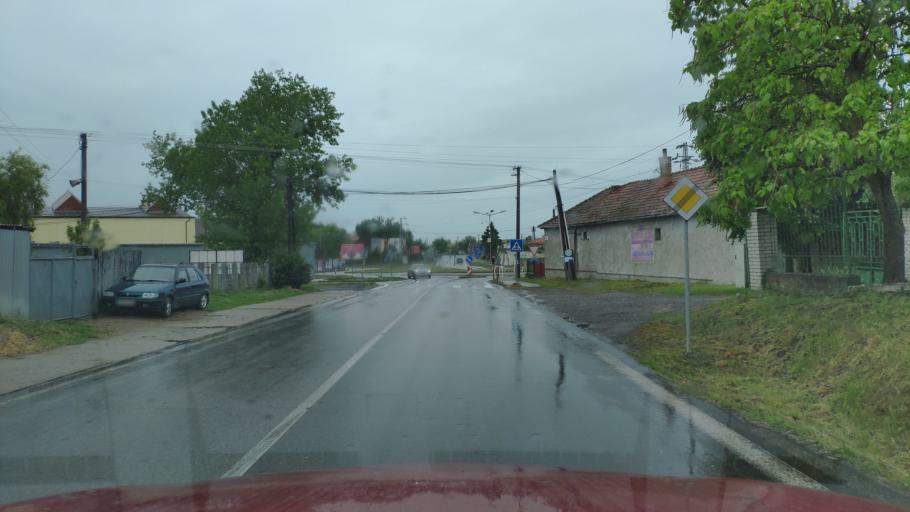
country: HU
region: Borsod-Abauj-Zemplen
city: Ricse
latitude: 48.4307
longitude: 21.9772
